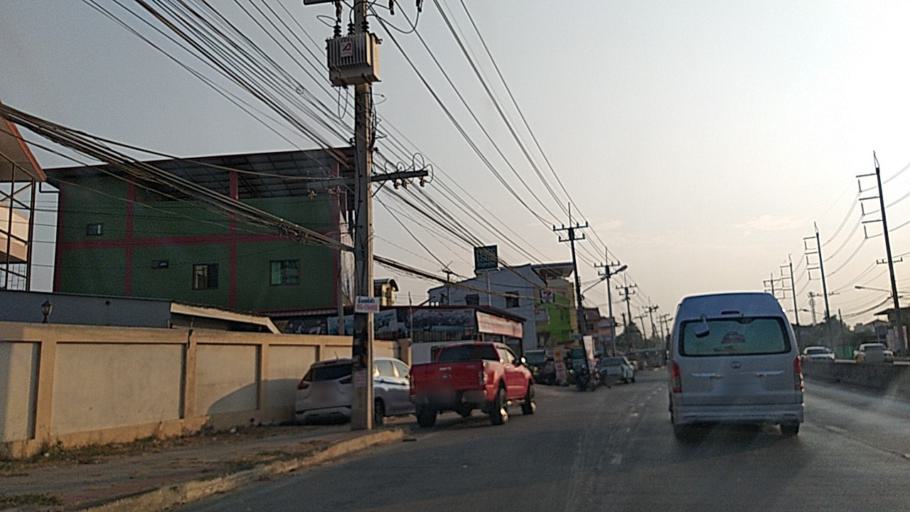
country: TH
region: Phra Nakhon Si Ayutthaya
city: Ban Bang Kadi Pathum Thani
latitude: 13.9969
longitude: 100.5551
